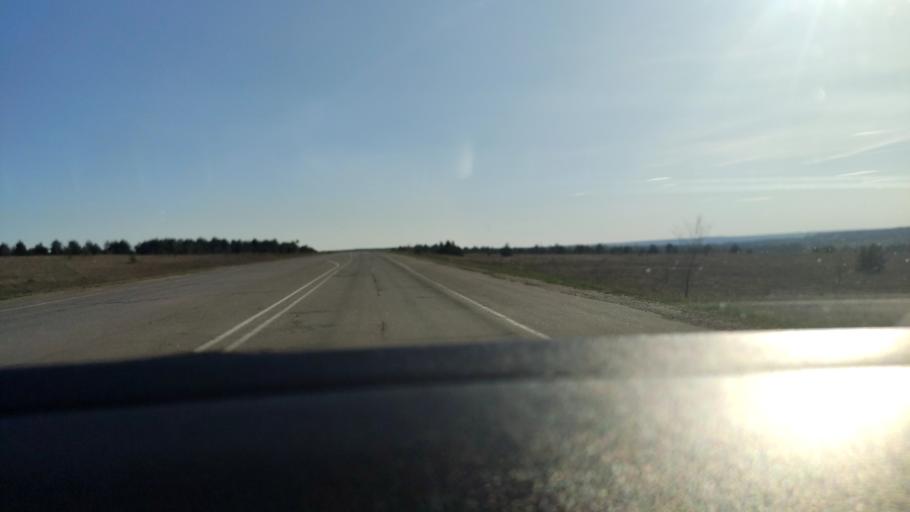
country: RU
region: Voronezj
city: Kolodeznyy
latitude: 51.3867
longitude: 39.2238
